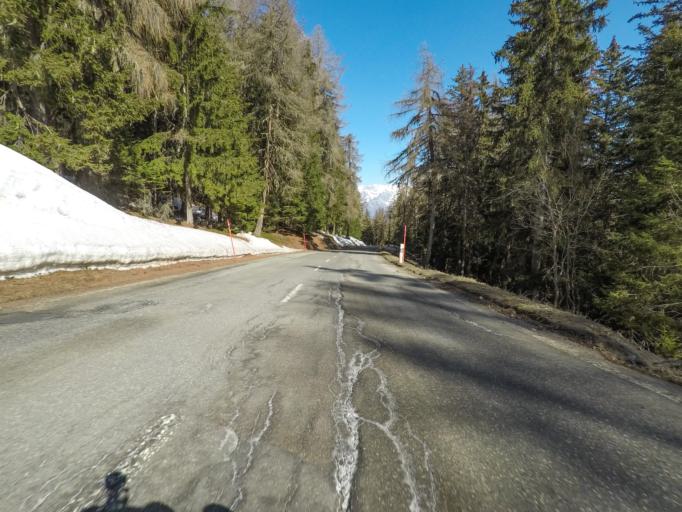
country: CH
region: Valais
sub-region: Herens District
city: Heremence
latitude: 46.1909
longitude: 7.3851
